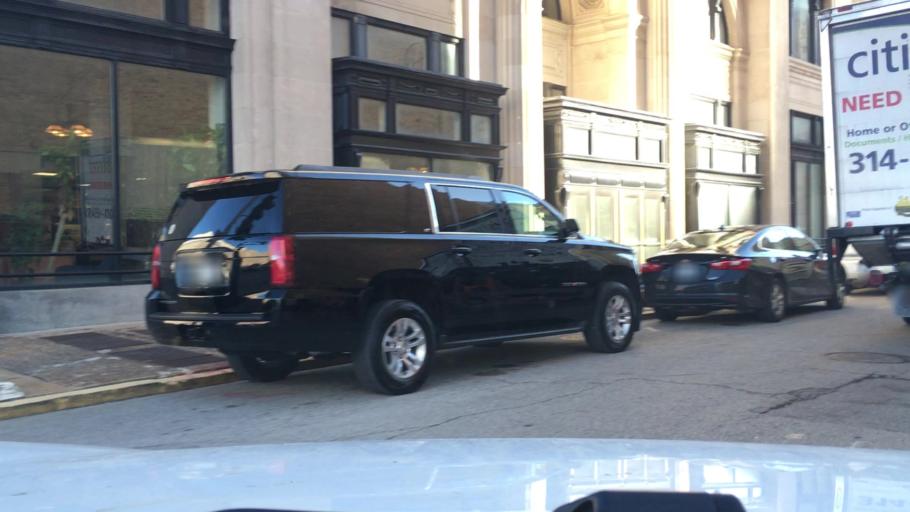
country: US
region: Missouri
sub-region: City of Saint Louis
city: St. Louis
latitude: 38.6296
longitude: -90.1973
